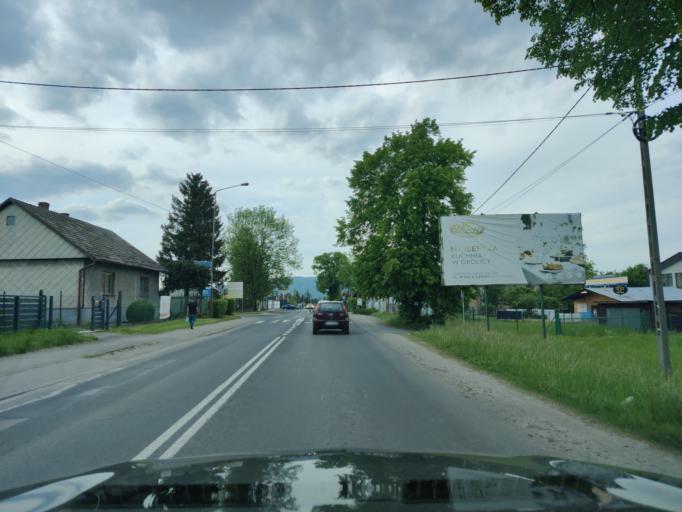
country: PL
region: Silesian Voivodeship
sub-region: Powiat zywiecki
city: Zywiec
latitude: 49.6877
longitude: 19.1834
